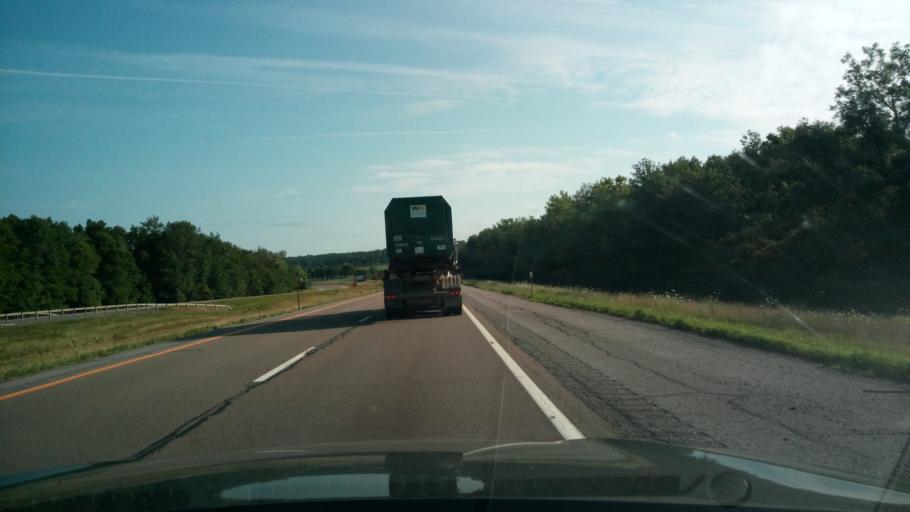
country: US
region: New York
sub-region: Livingston County
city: Mount Morris
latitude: 42.7203
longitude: -77.8318
